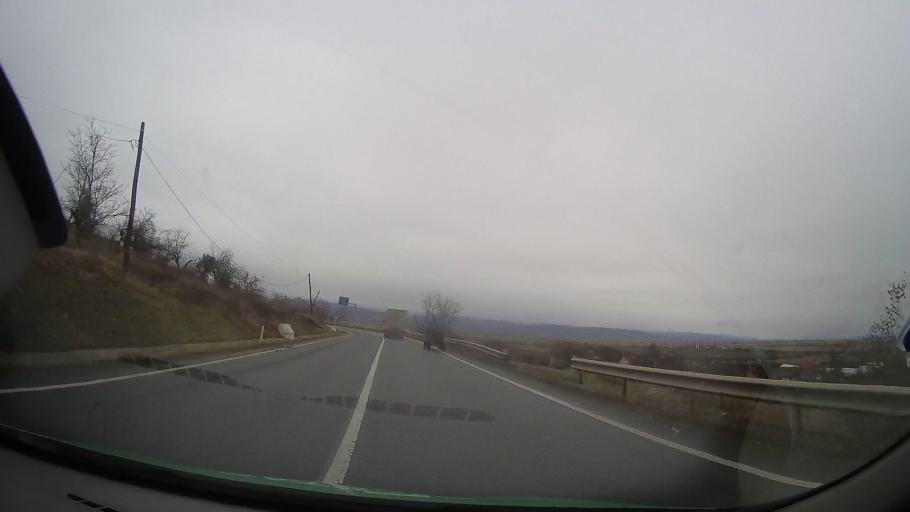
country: RO
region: Mures
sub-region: Comuna Breaza
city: Breaza
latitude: 46.7620
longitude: 24.6599
